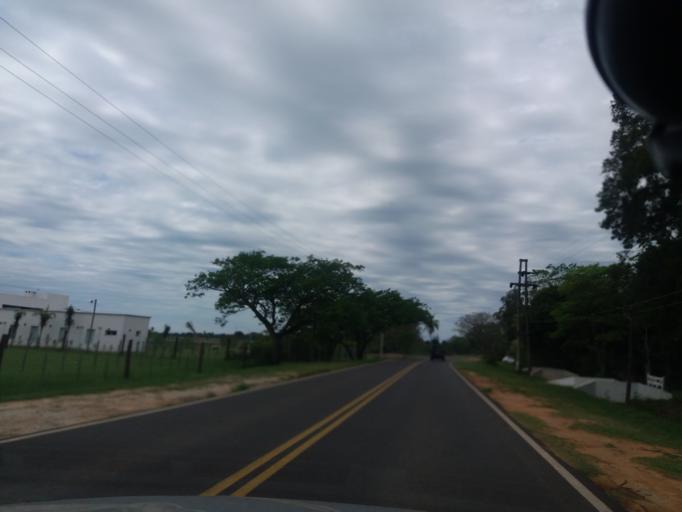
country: AR
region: Corrientes
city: Corrientes
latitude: -27.4564
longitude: -58.7153
